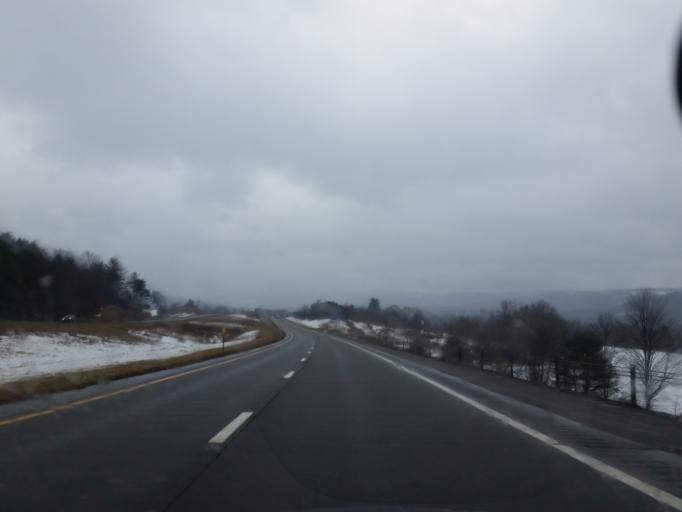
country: US
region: New York
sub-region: Chenango County
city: Lakeview
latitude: 42.3542
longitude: -75.9911
